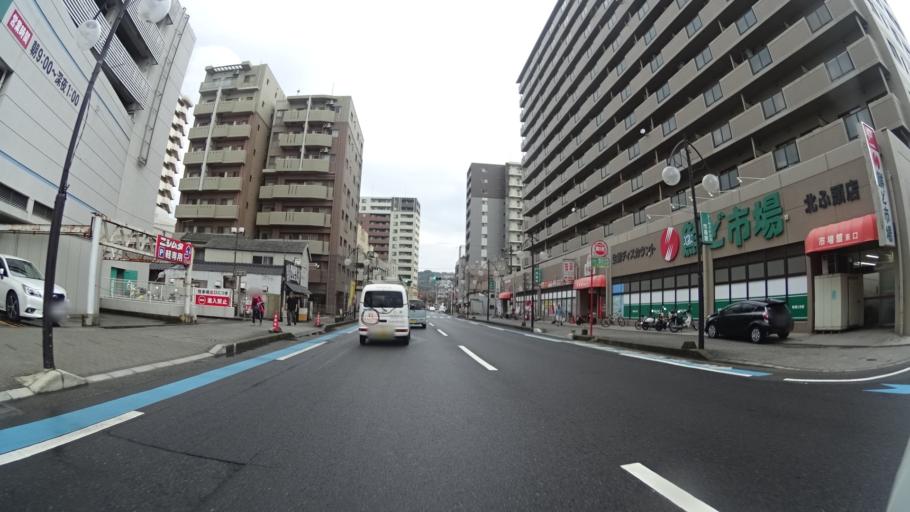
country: JP
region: Kagoshima
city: Kagoshima-shi
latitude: 31.5989
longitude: 130.5619
